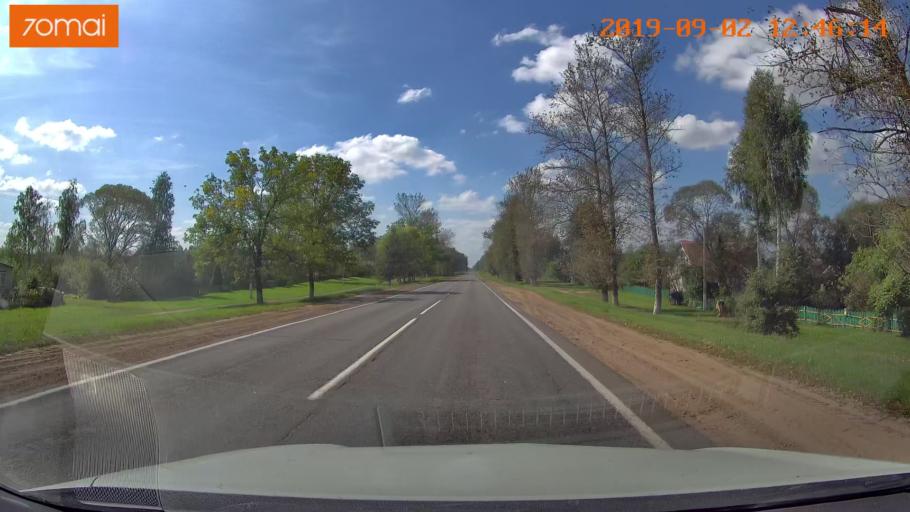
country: RU
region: Smolensk
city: Shumyachi
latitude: 53.7533
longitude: 32.2218
